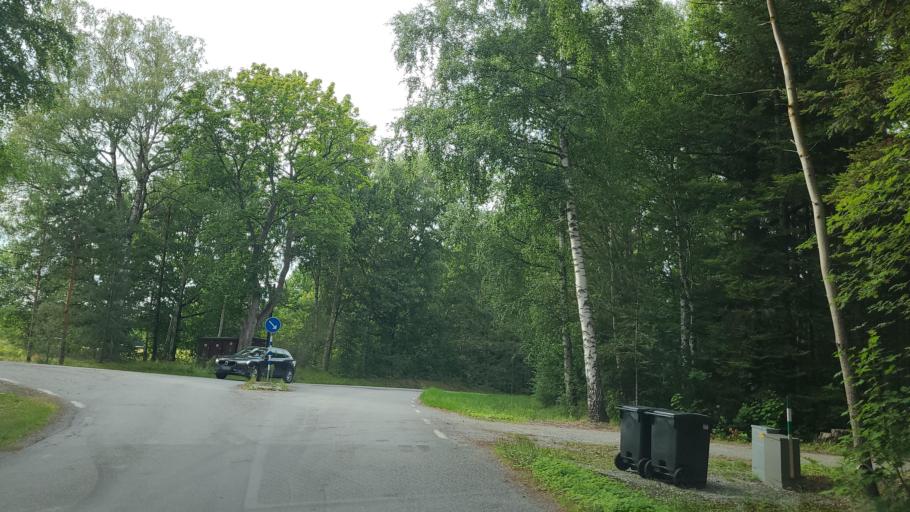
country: SE
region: Stockholm
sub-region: Upplands-Bro Kommun
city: Bro
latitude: 59.4881
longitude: 17.5683
